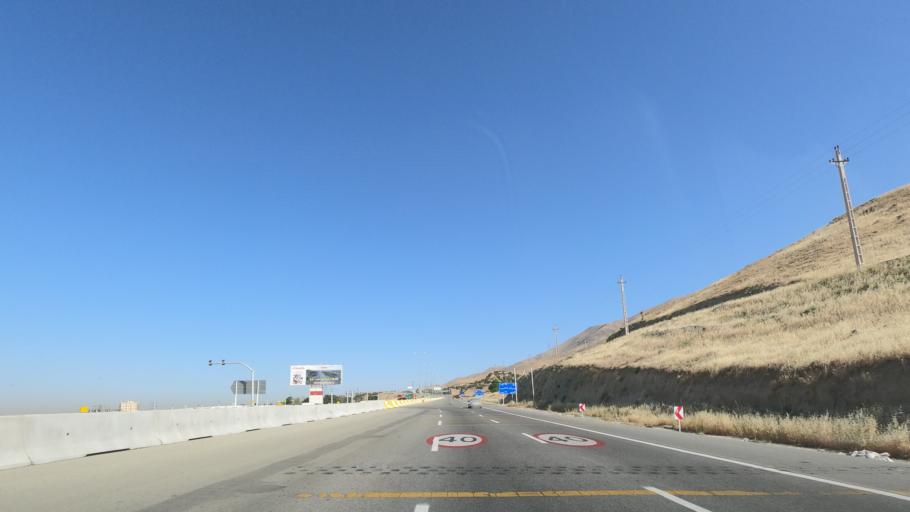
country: IR
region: Tehran
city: Shahr-e Qods
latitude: 35.7570
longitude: 51.0793
